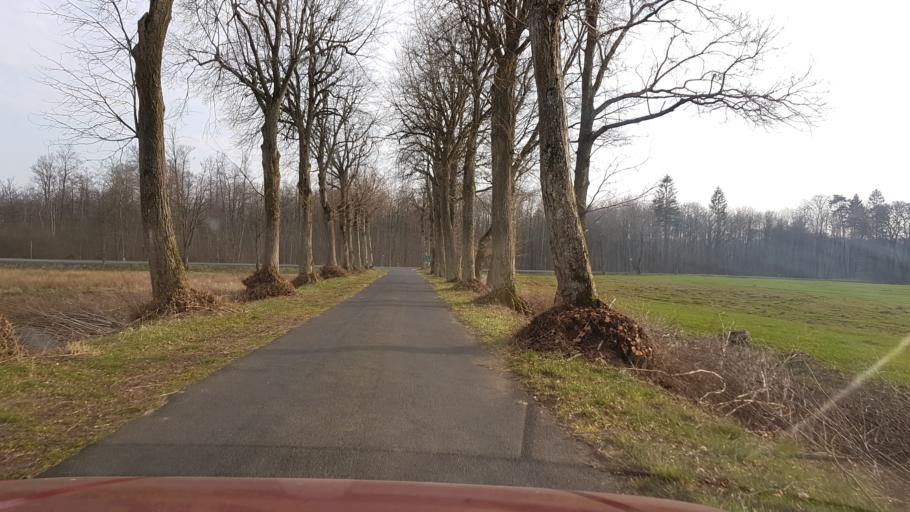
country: PL
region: West Pomeranian Voivodeship
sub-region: Powiat bialogardzki
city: Bialogard
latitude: 54.0812
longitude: 15.9753
